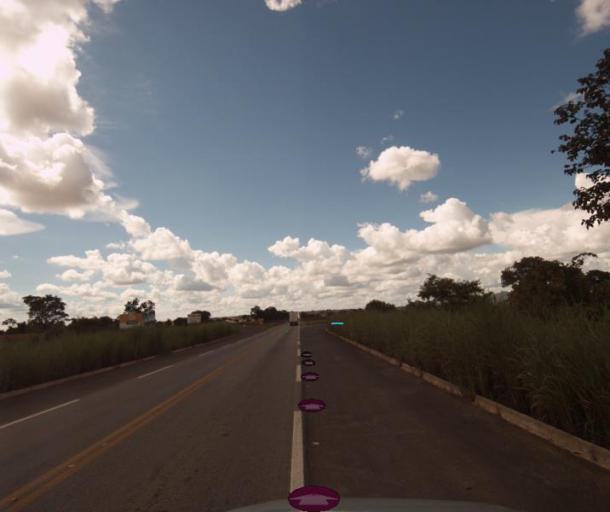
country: BR
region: Goias
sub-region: Porangatu
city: Porangatu
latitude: -13.4850
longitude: -49.1364
